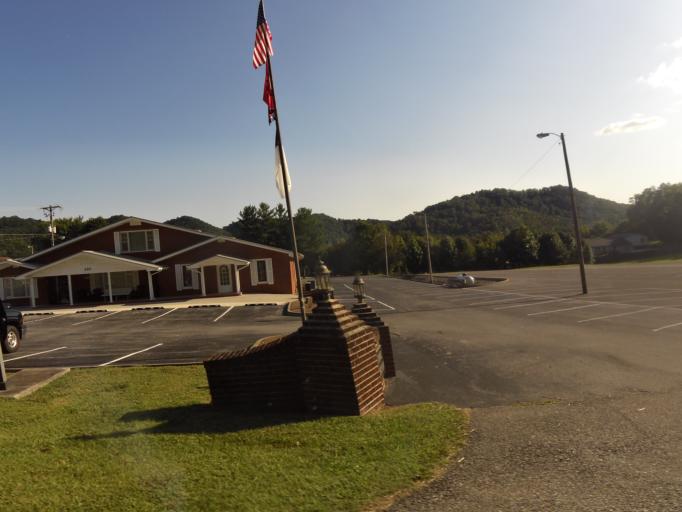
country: US
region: Tennessee
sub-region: Union County
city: Maynardville
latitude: 36.2619
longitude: -83.7762
